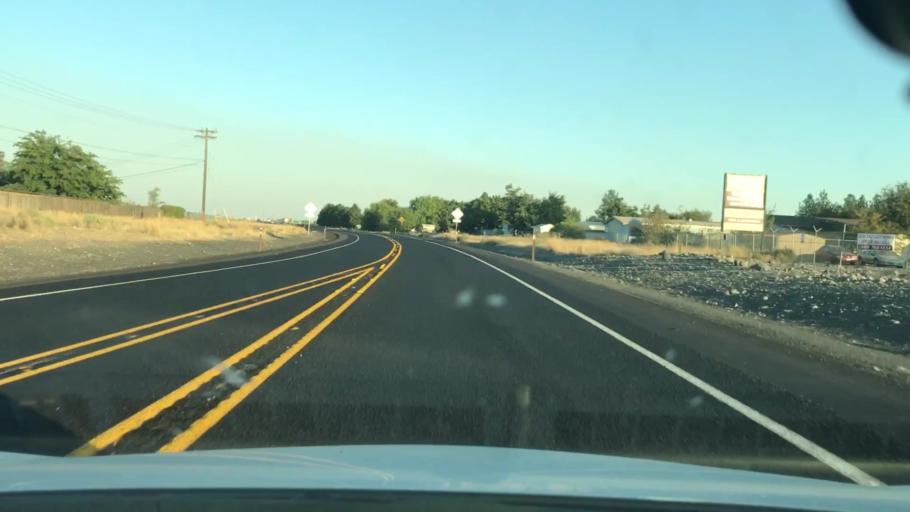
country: US
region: Washington
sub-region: Grant County
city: Cascade Valley
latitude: 47.1609
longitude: -119.3225
